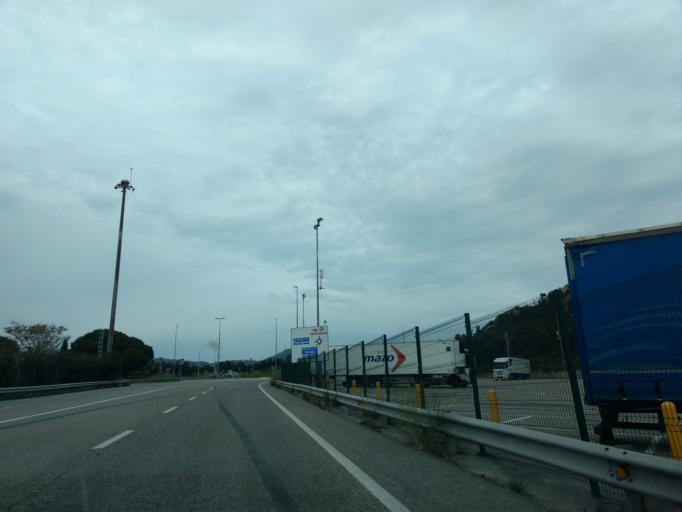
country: ES
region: Catalonia
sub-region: Provincia de Girona
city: la Jonquera
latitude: 42.4321
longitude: 2.8665
